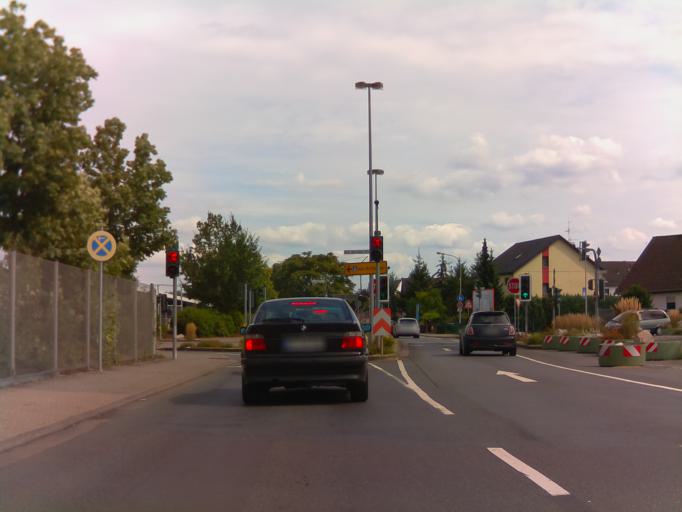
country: DE
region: Hesse
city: Weiterstadt
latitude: 49.8936
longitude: 8.6103
